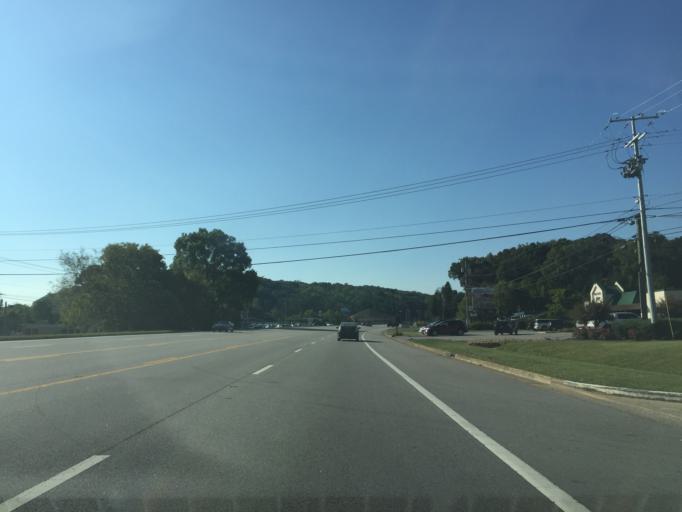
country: US
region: Tennessee
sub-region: Hamilton County
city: Harrison
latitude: 35.1233
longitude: -85.1252
